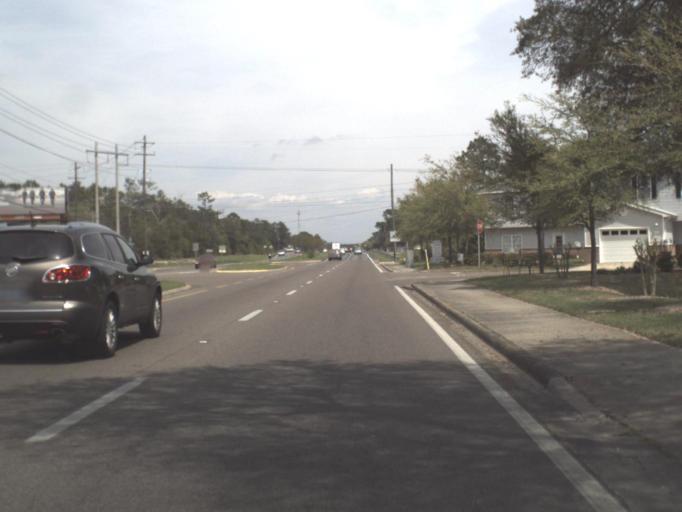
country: US
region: Florida
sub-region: Okaloosa County
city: Wright
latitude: 30.4617
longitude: -86.6268
